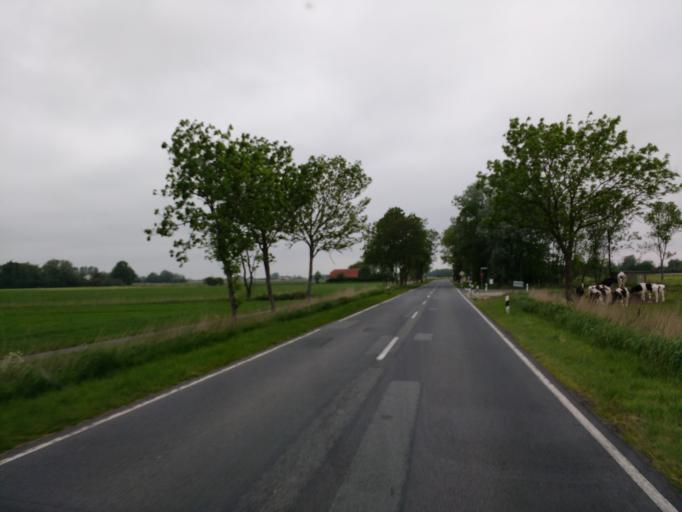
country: DE
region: Lower Saxony
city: Jever
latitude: 53.6489
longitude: 7.9213
